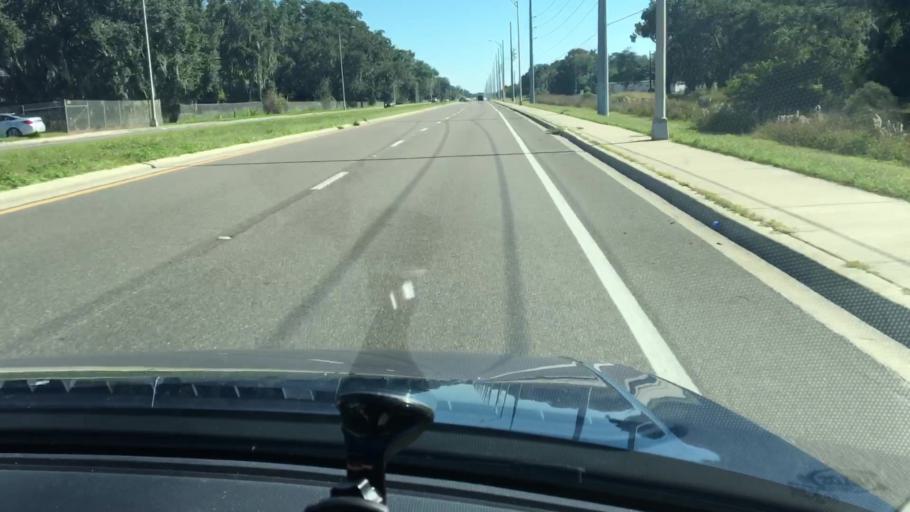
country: US
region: Florida
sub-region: Polk County
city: Kathleen
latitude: 28.1159
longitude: -82.0217
